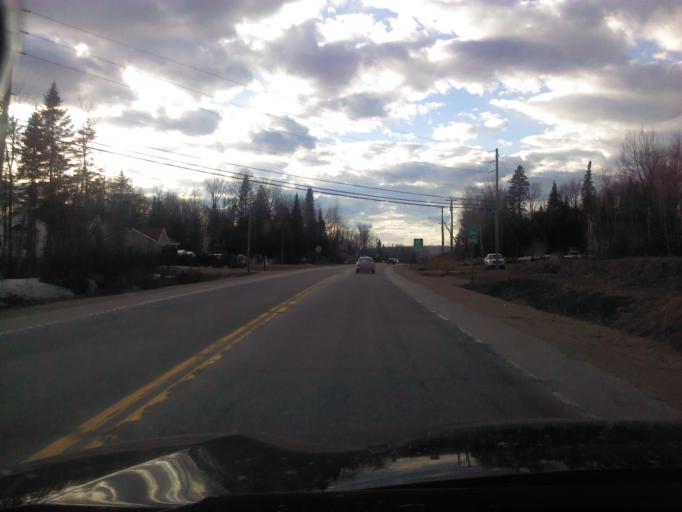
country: CA
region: Quebec
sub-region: Capitale-Nationale
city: Sainte Catherine de la Jacques Cartier
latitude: 46.8282
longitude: -71.5931
